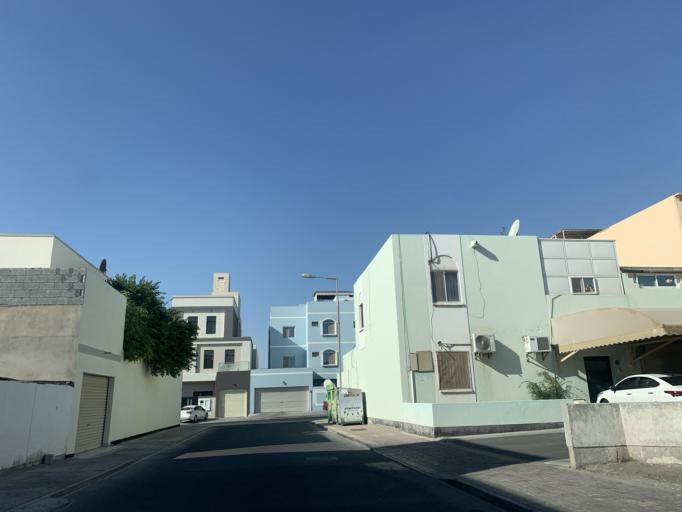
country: BH
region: Central Governorate
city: Madinat Hamad
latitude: 26.1153
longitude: 50.5067
